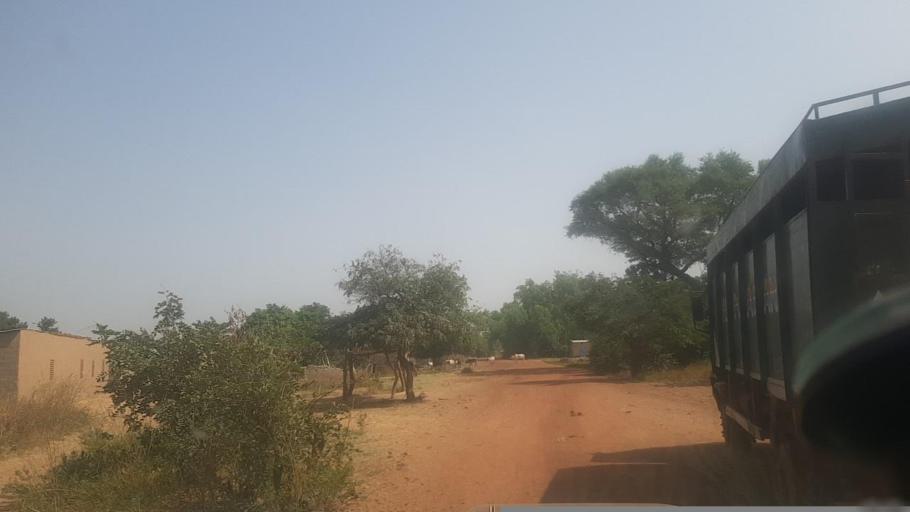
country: ML
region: Segou
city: Bla
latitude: 12.9130
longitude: -6.2465
